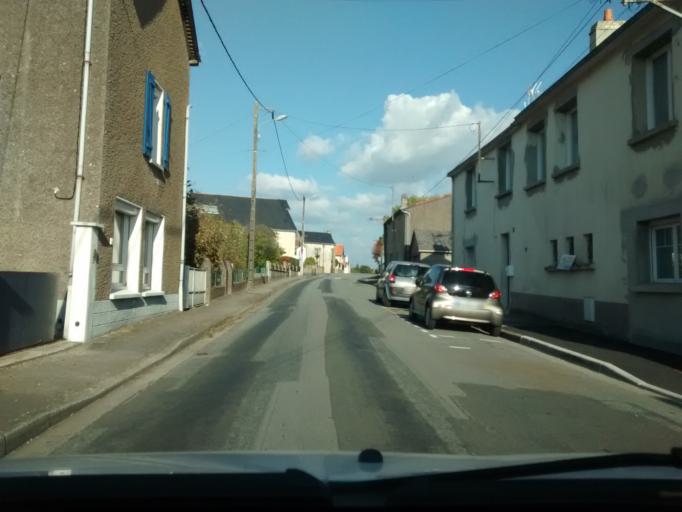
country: FR
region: Pays de la Loire
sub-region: Departement de la Loire-Atlantique
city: Sautron
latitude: 47.2637
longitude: -1.6751
